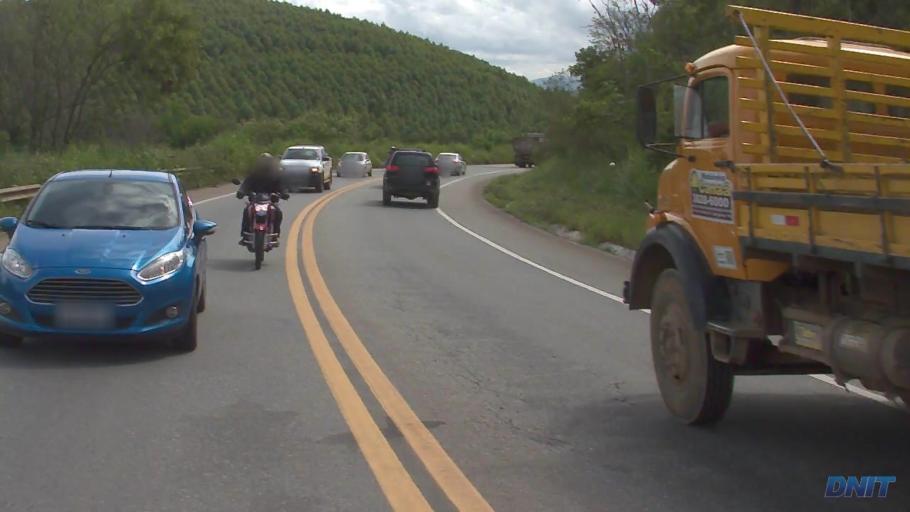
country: BR
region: Minas Gerais
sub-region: Ipaba
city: Ipaba
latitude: -19.3608
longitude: -42.4472
